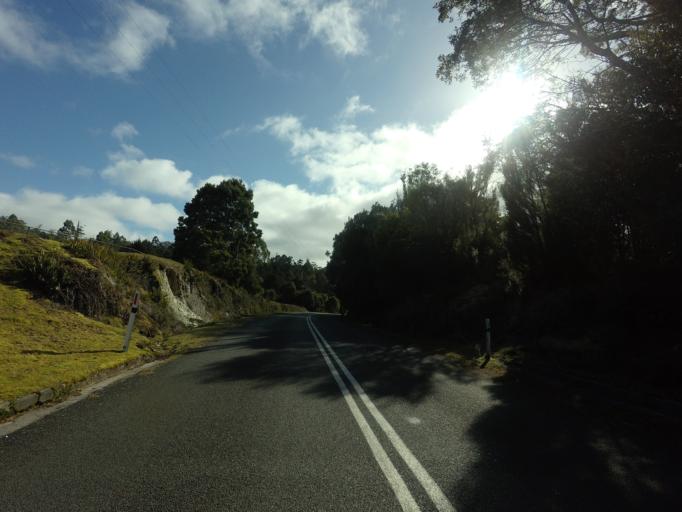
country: AU
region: Tasmania
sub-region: West Coast
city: Queenstown
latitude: -42.7666
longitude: 146.0453
